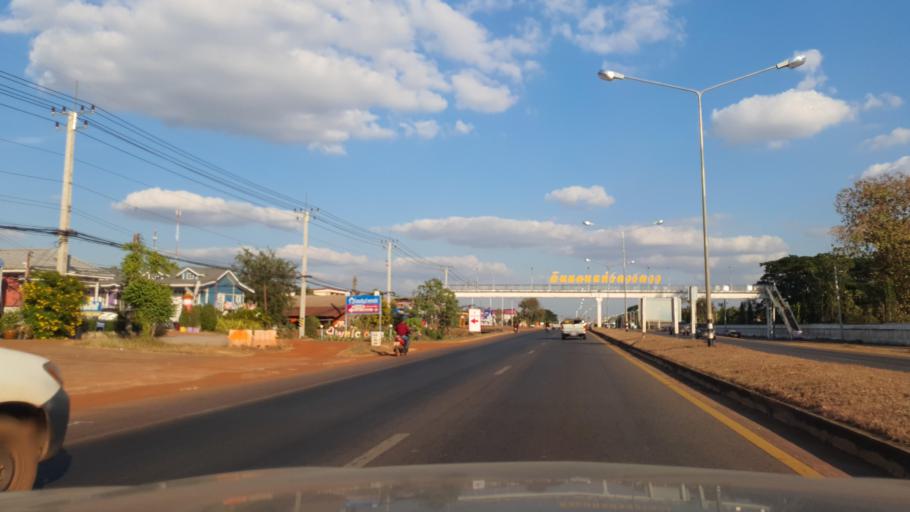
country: TH
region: Sakon Nakhon
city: Sakon Nakhon
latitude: 17.2567
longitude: 104.1711
